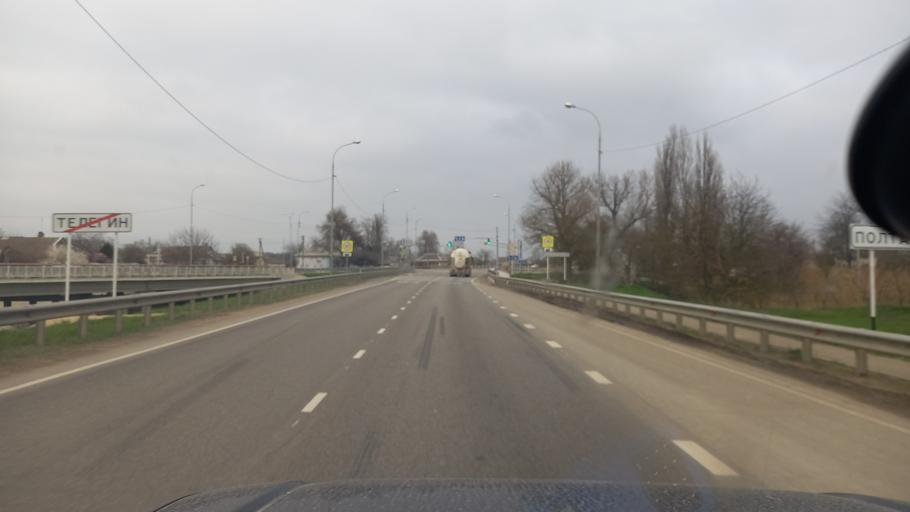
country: RU
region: Krasnodarskiy
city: Krasnoarmeyskaya
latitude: 45.2826
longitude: 38.2430
